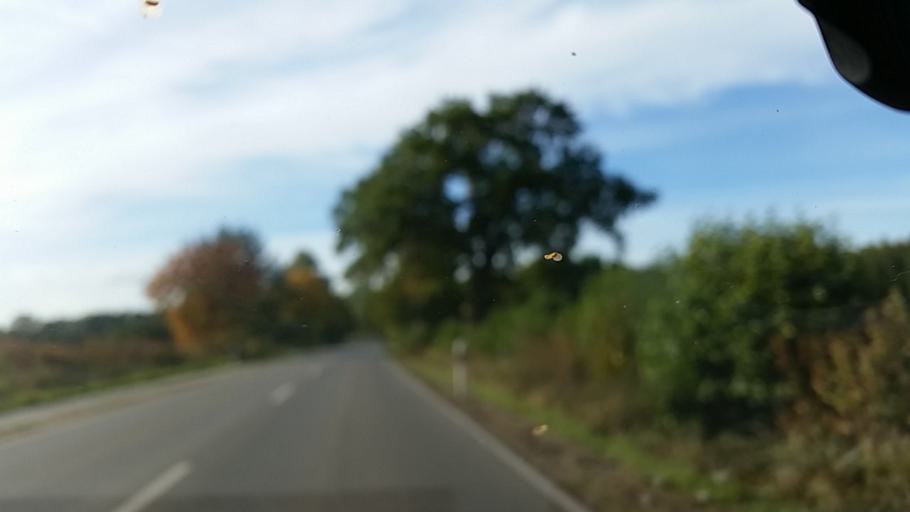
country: DE
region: Schleswig-Holstein
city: Jersbek
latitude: 53.7374
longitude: 10.2339
